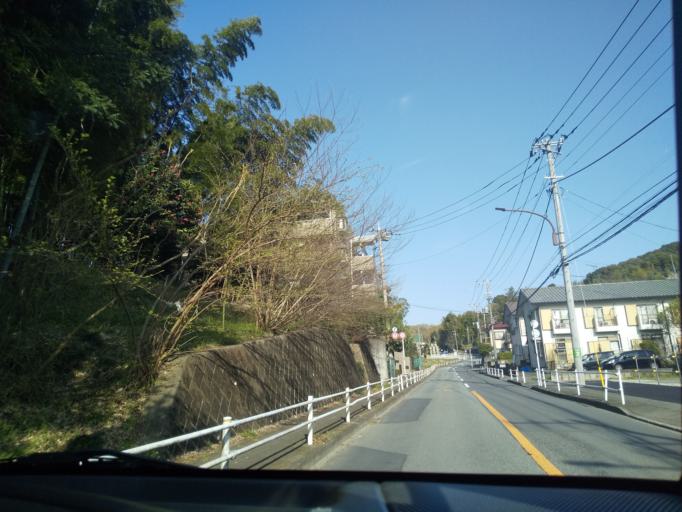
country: JP
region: Tokyo
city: Hino
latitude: 35.6435
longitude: 139.4256
